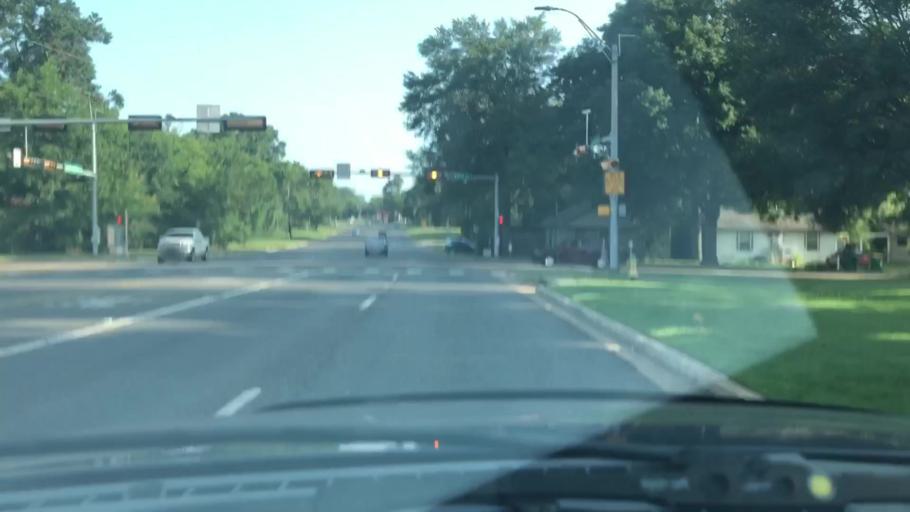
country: US
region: Texas
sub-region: Bowie County
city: Texarkana
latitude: 33.4288
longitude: -94.0613
